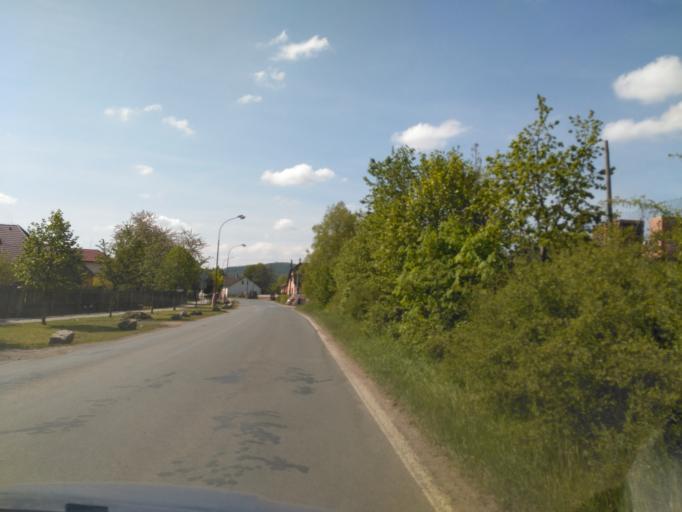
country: CZ
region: Central Bohemia
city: Lochovice
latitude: 49.8484
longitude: 13.9759
